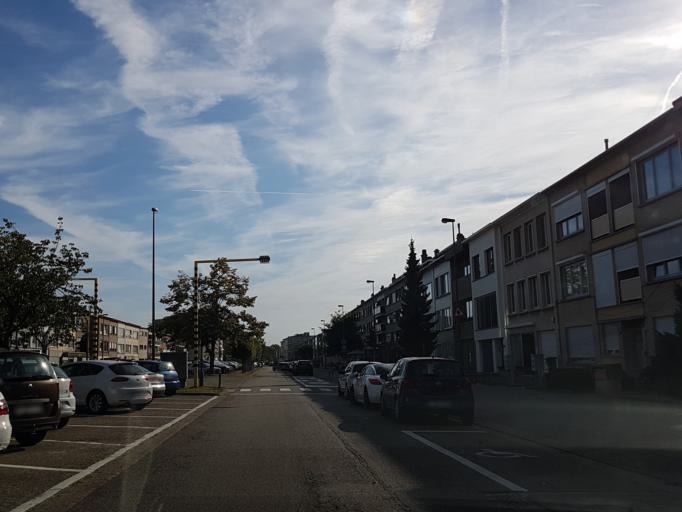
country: BE
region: Flanders
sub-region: Provincie Antwerpen
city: Antwerpen
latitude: 51.2504
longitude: 4.4334
